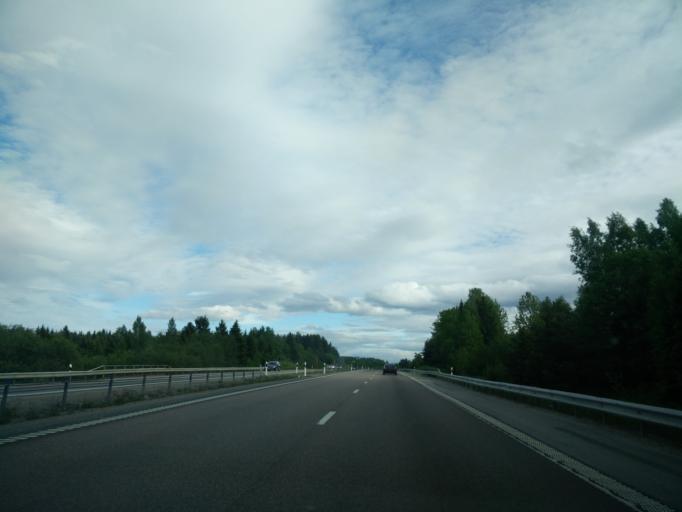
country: SE
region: Vaesternorrland
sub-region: Sundsvalls Kommun
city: Sundsbruk
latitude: 62.4345
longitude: 17.3408
